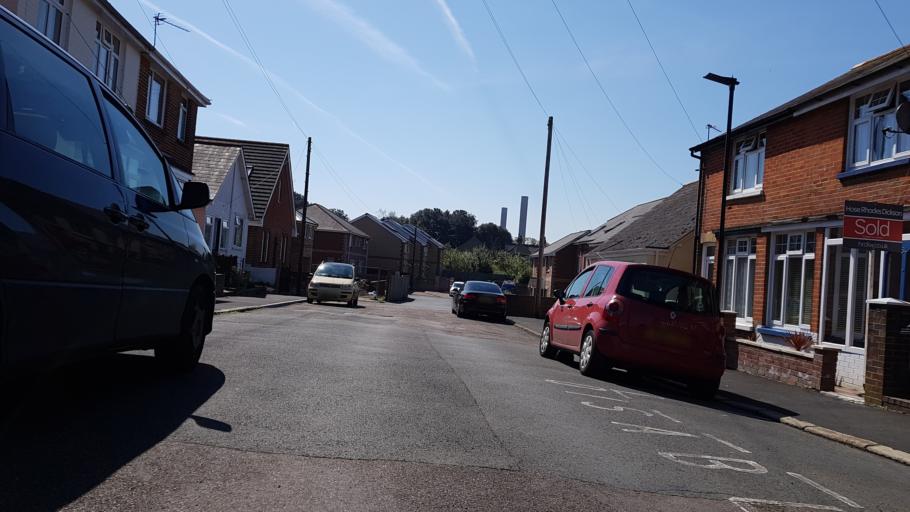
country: GB
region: England
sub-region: Isle of Wight
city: East Cowes
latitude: 50.7529
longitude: -1.2854
